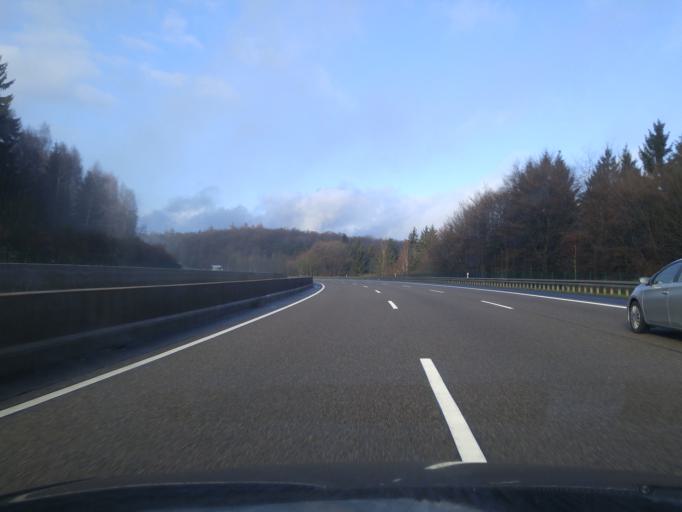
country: DE
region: Hesse
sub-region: Regierungsbezirk Kassel
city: Kirchheim
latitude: 50.8791
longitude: 9.6009
